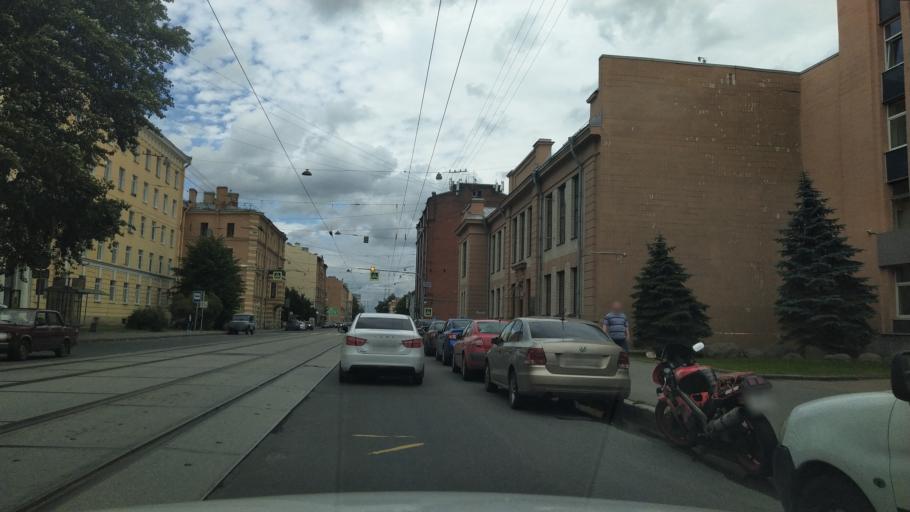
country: RU
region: Leningrad
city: Finlyandskiy
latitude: 59.9631
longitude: 30.3799
